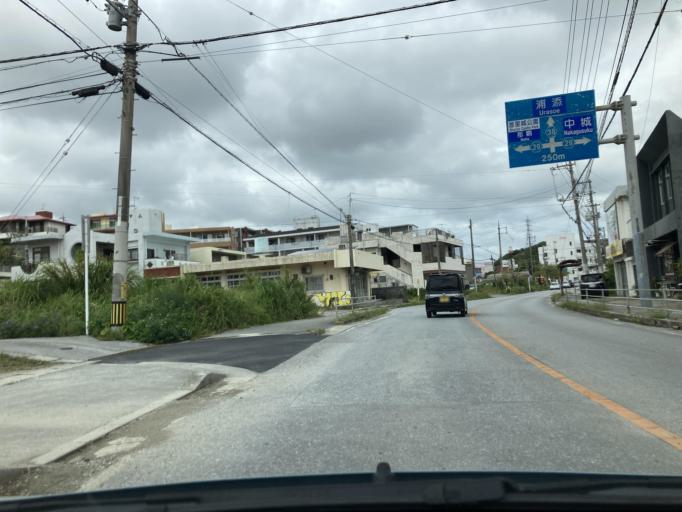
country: JP
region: Okinawa
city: Ginowan
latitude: 26.2367
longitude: 127.7502
